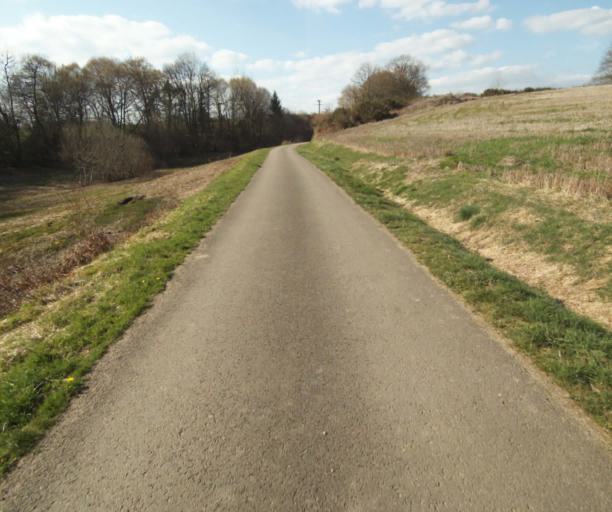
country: FR
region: Limousin
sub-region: Departement de la Correze
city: Saint-Mexant
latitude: 45.3225
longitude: 1.6180
